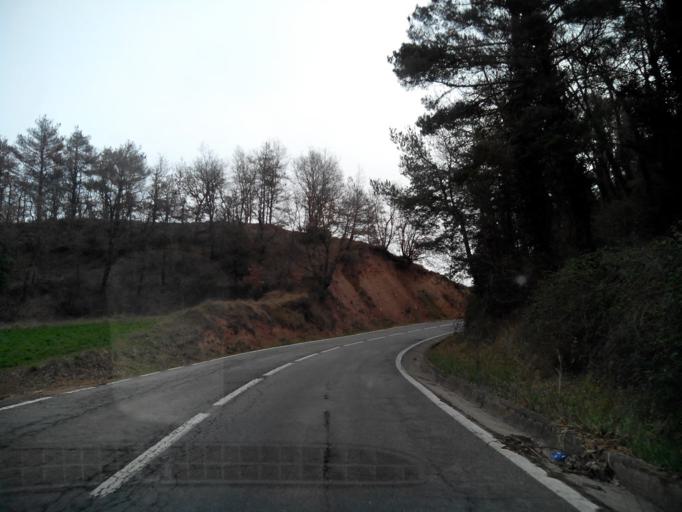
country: ES
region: Catalonia
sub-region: Provincia de Barcelona
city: Olost
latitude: 41.9697
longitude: 2.1387
